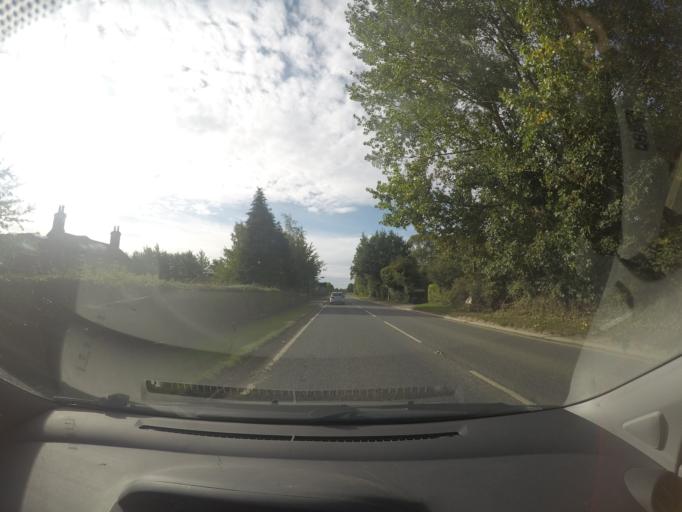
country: GB
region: England
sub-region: North Yorkshire
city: Riccall
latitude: 53.8559
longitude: -1.0495
